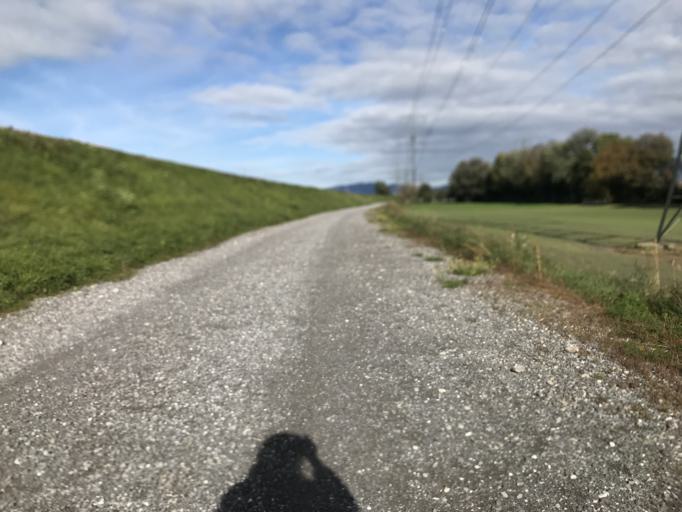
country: AT
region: Vorarlberg
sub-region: Politischer Bezirk Feldkirch
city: Mader
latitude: 47.3505
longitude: 9.6062
